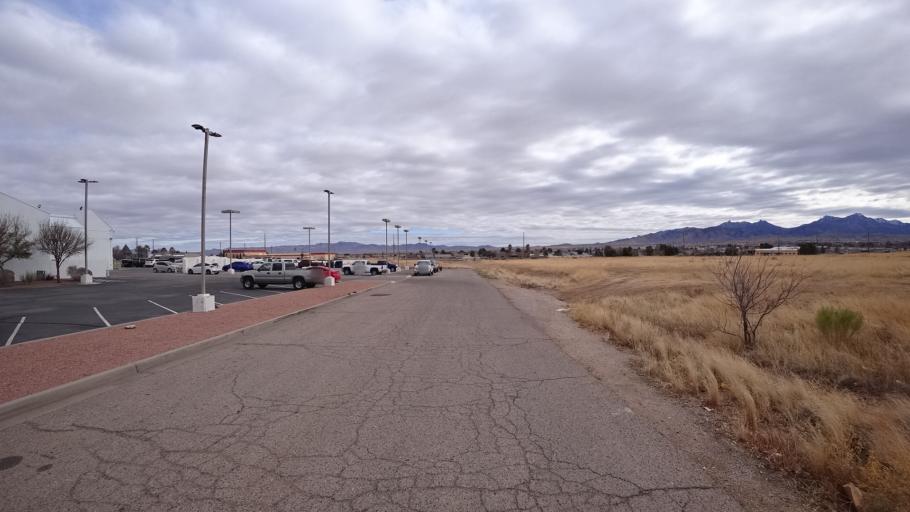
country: US
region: Arizona
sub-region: Mohave County
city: New Kingman-Butler
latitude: 35.2308
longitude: -114.0361
